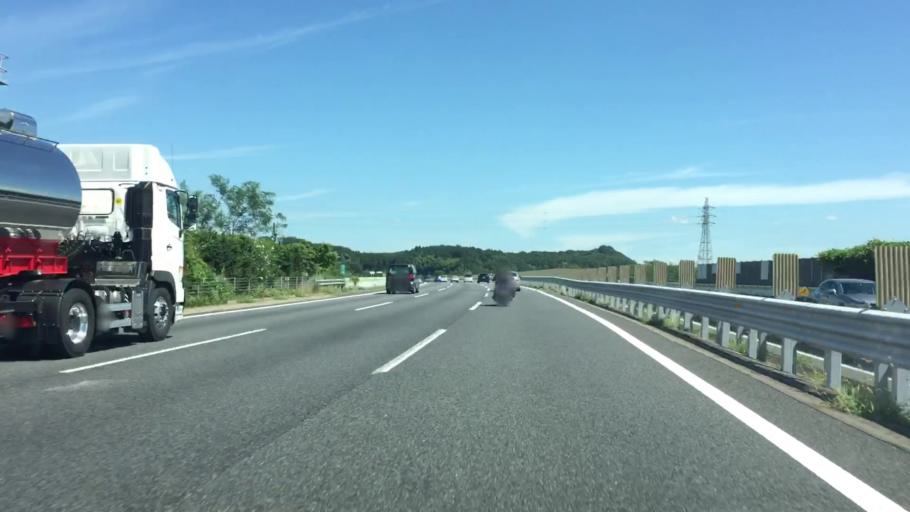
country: JP
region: Tochigi
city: Kanuma
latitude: 36.4779
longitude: 139.7493
